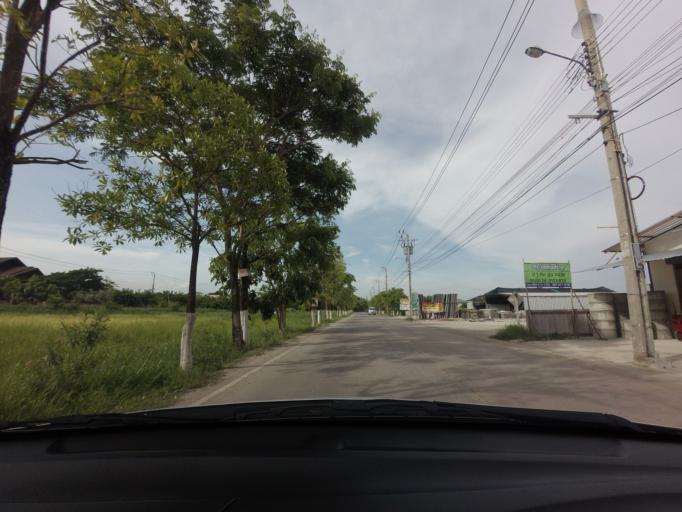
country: TH
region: Bangkok
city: Bang Na
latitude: 13.6413
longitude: 100.6605
